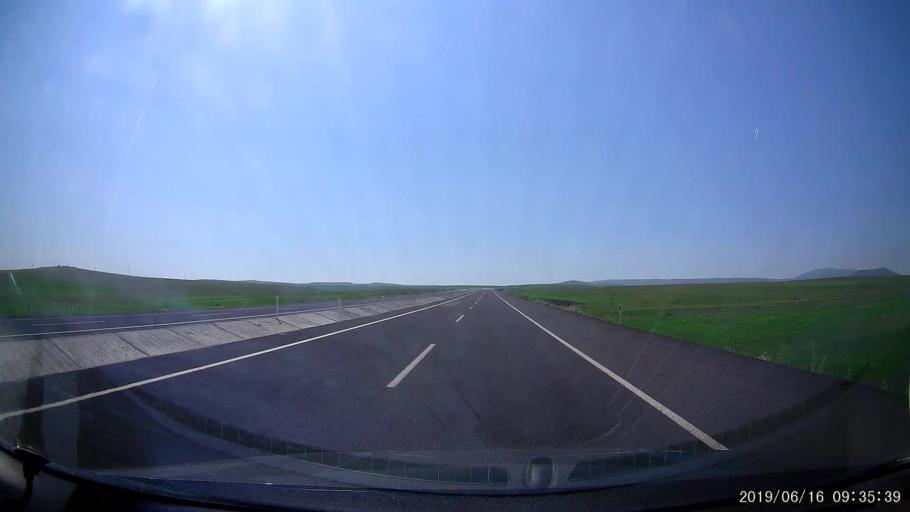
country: TR
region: Kars
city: Kars
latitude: 40.5687
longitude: 43.1593
